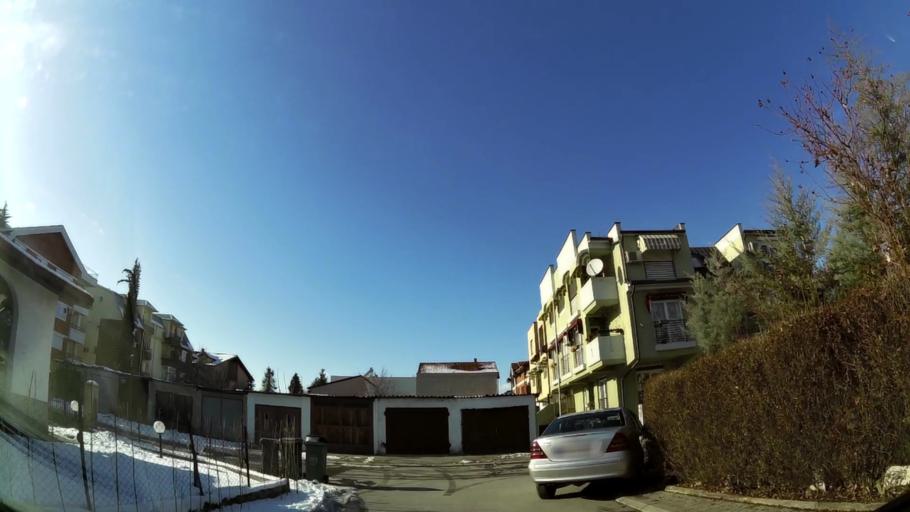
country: MK
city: Krushopek
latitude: 42.0043
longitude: 21.3760
